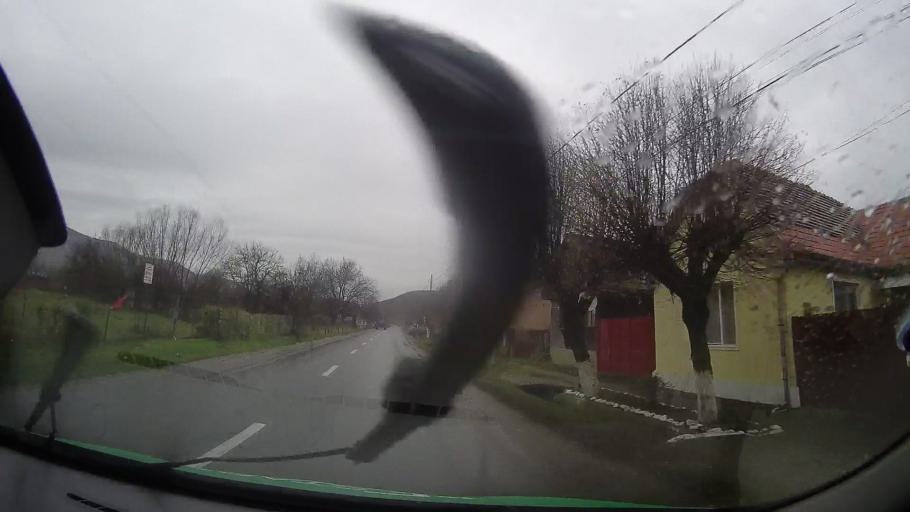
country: RO
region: Bistrita-Nasaud
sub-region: Comuna Mariselu
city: Mariselu
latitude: 47.0405
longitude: 24.4741
